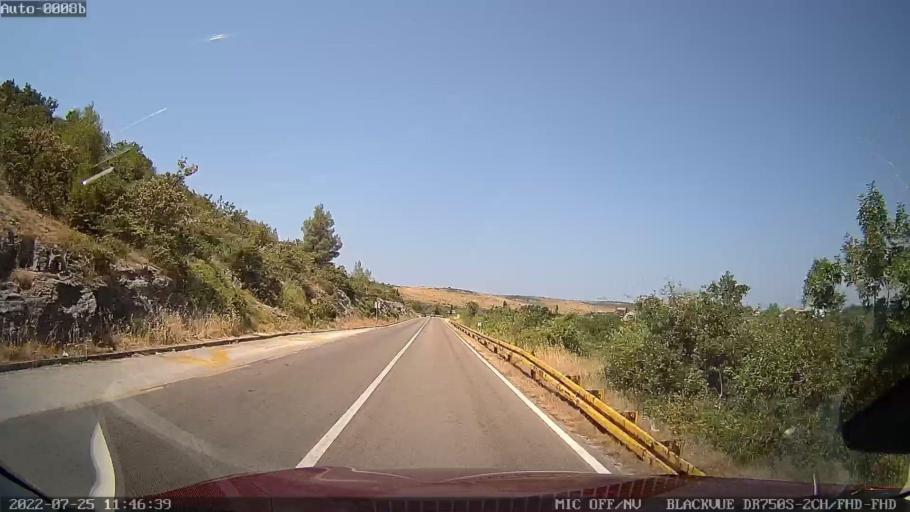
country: HR
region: Zadarska
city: Razanac
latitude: 44.2421
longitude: 15.3052
